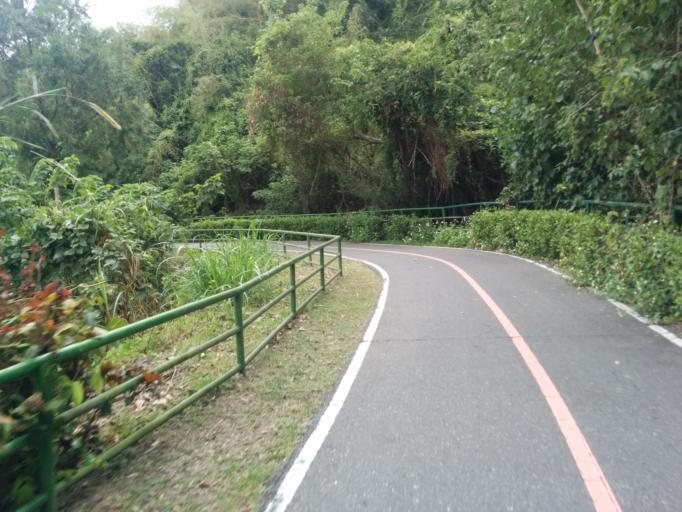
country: TW
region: Taiwan
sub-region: Taitung
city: Taitung
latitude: 23.0529
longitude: 121.1564
